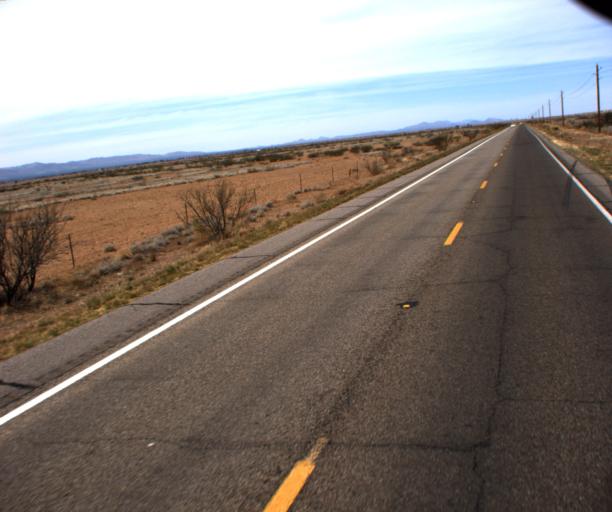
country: US
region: Arizona
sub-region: Cochise County
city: Pirtleville
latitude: 31.4252
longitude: -109.5827
